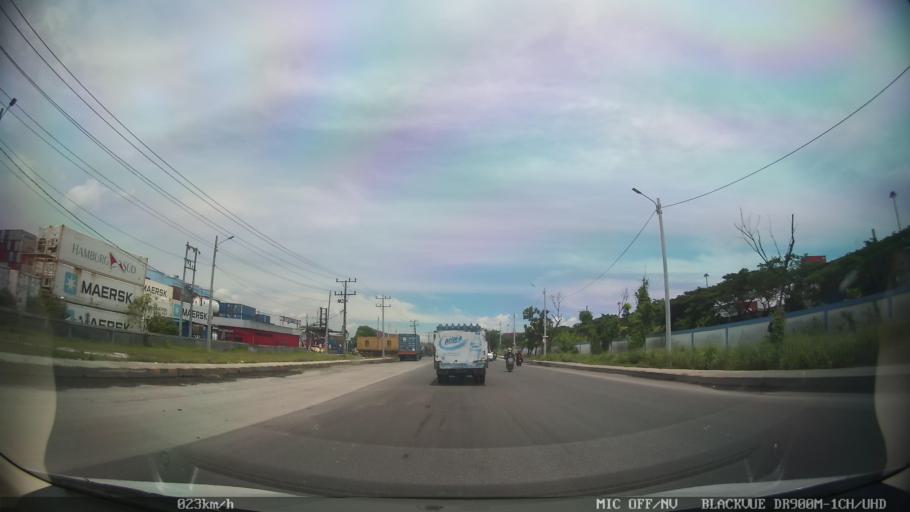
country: ID
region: North Sumatra
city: Belawan
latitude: 3.7787
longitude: 98.6990
